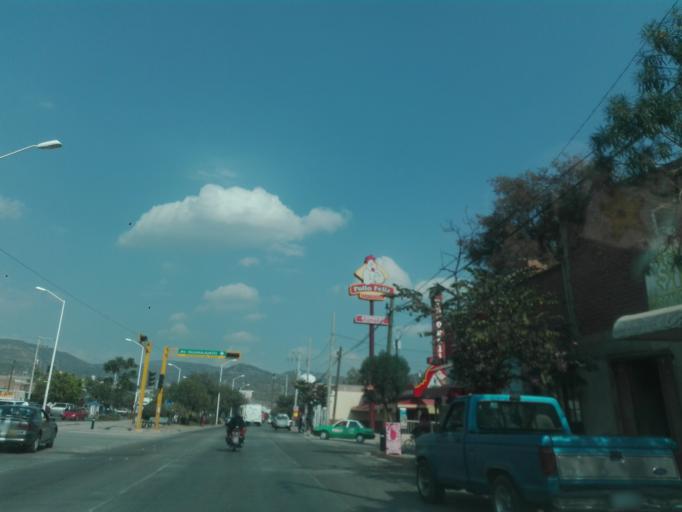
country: MX
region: Guanajuato
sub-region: Leon
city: Fraccionamiento Paraiso Real
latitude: 21.1173
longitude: -101.6017
